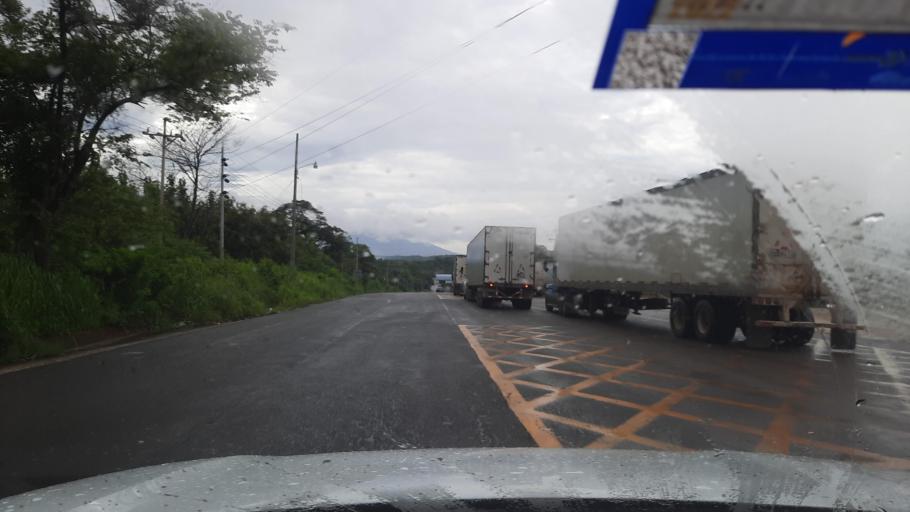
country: NI
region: Rivas
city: Cardenas
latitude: 11.1967
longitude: -85.6211
